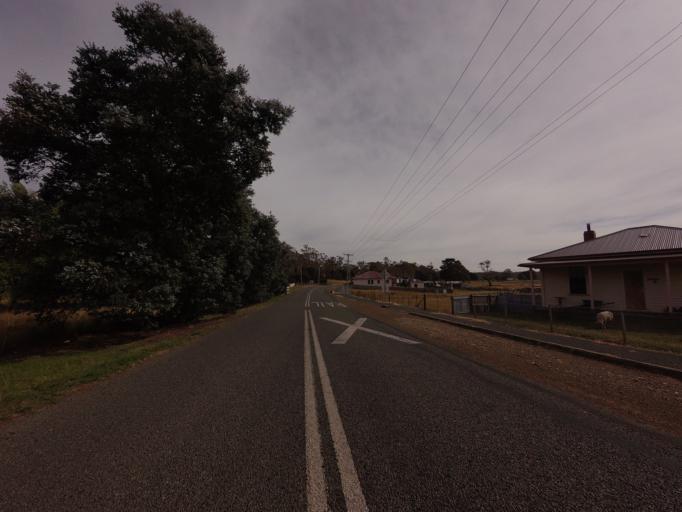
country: AU
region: Tasmania
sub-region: Brighton
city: Bridgewater
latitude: -42.3486
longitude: 147.4049
